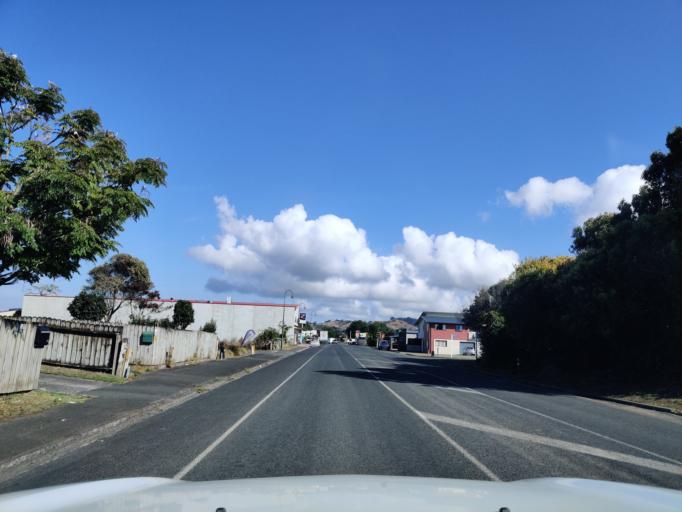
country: NZ
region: Auckland
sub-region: Auckland
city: Pukekohe East
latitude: -37.2473
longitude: 175.0246
